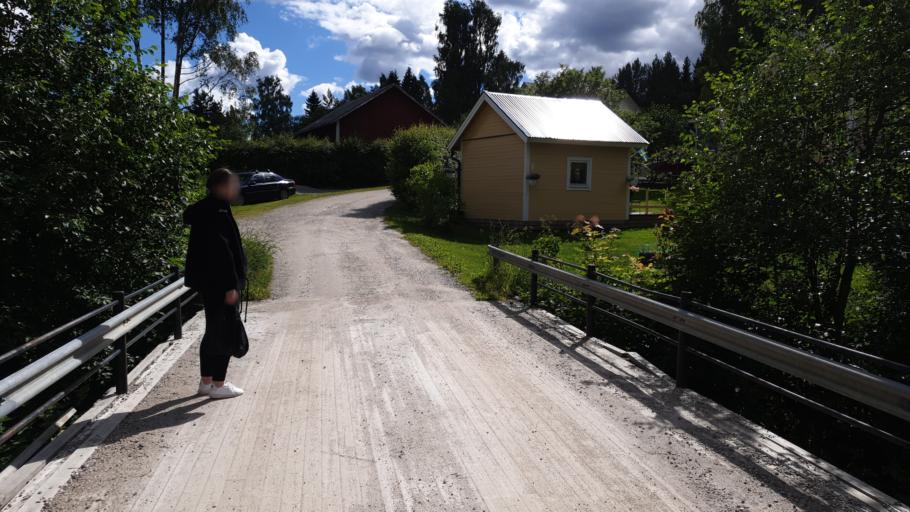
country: SE
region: Gaevleborg
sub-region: Nordanstigs Kommun
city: Bergsjoe
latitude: 62.0404
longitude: 17.0880
